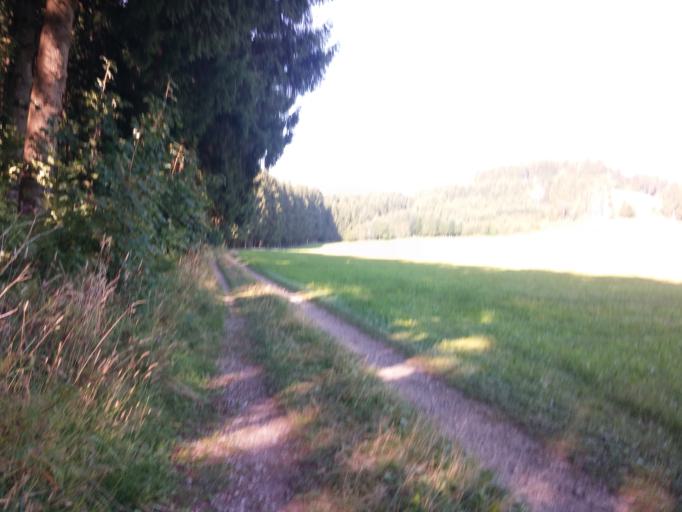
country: DE
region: Baden-Wuerttemberg
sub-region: Tuebingen Region
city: Leutkirch im Allgau
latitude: 47.7774
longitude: 10.0710
